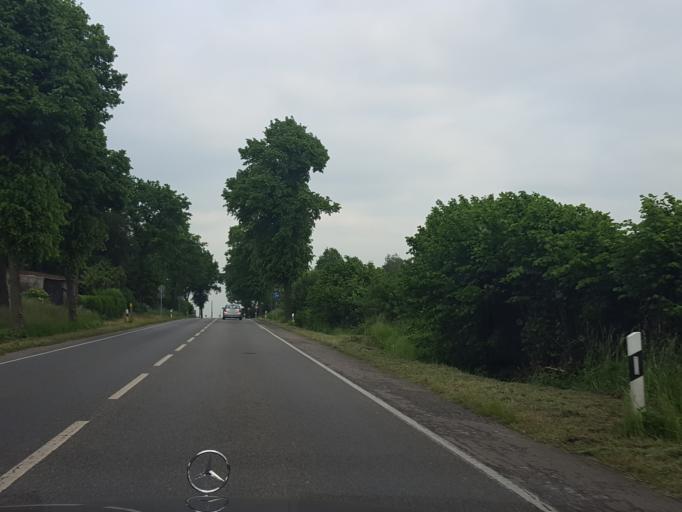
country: DE
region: North Rhine-Westphalia
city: Oer-Erkenschwick
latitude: 51.6300
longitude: 7.2402
